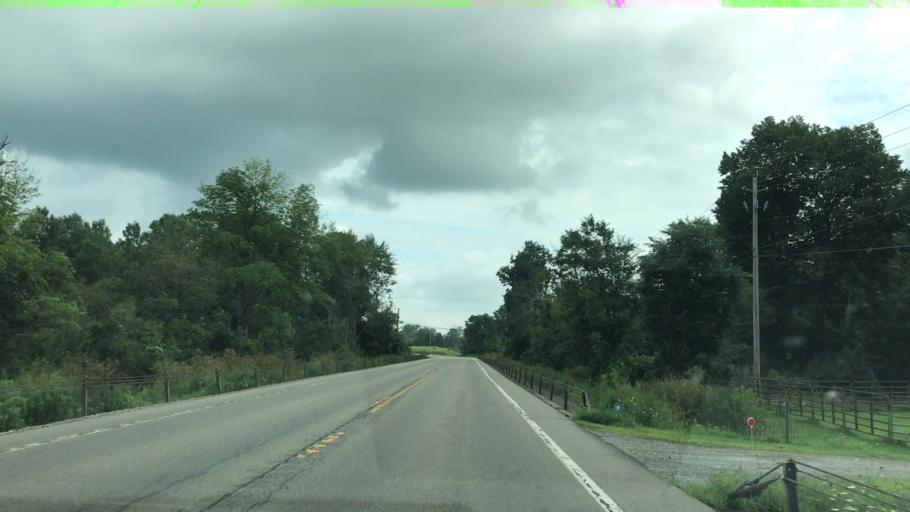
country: US
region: New York
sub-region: Steuben County
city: Bath
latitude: 42.4180
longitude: -77.3412
